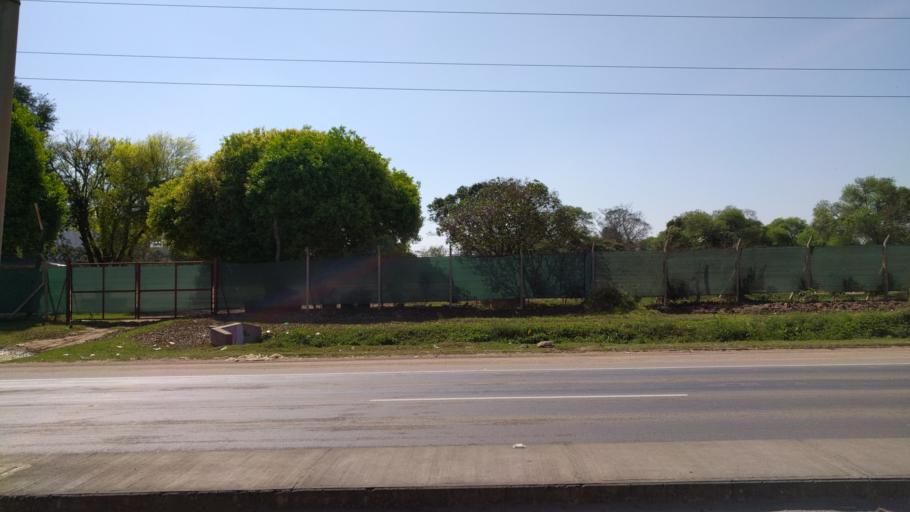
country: BO
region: Santa Cruz
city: Cotoca
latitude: -17.7626
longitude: -63.0261
